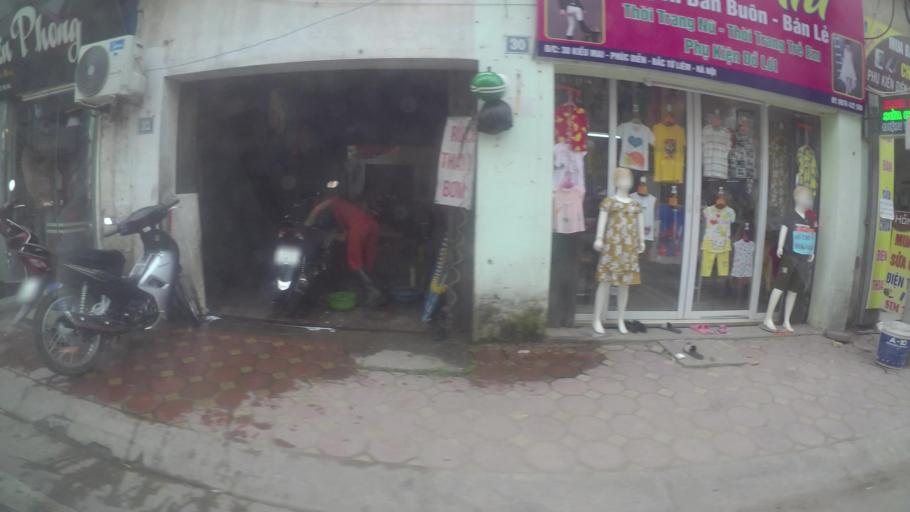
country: VN
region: Ha Noi
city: Cau Dien
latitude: 21.0435
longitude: 105.7524
